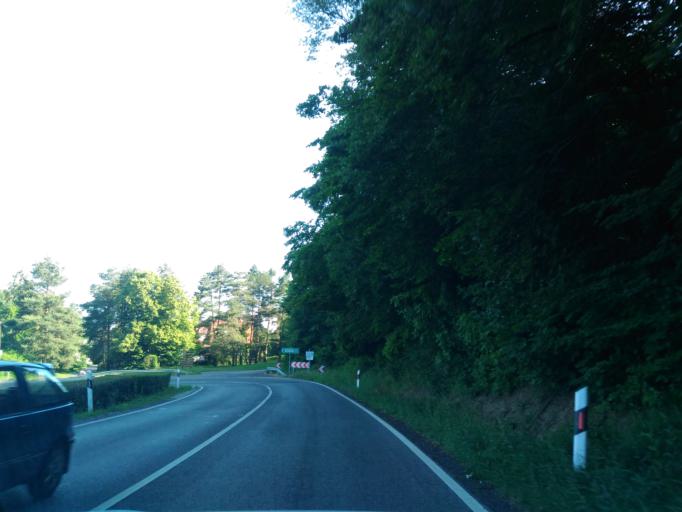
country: HU
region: Baranya
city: Komlo
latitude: 46.1825
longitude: 18.2624
